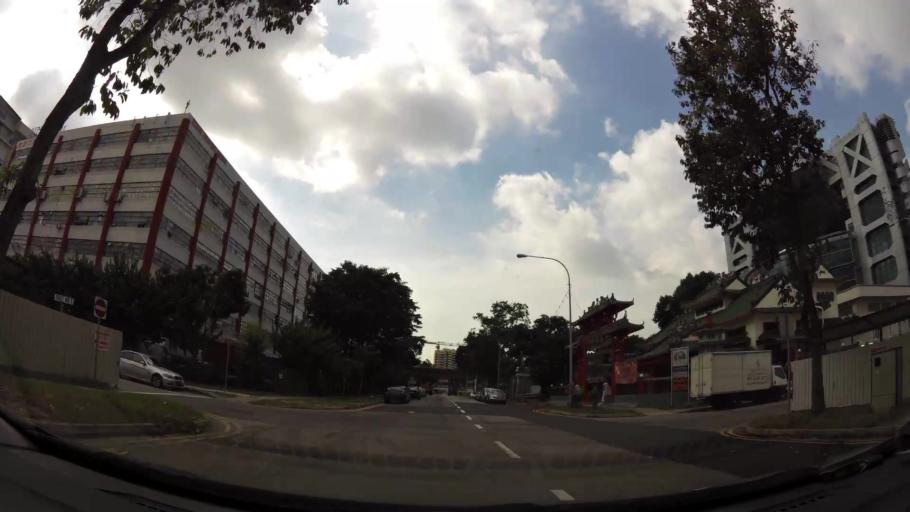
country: SG
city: Singapore
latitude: 1.3200
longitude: 103.8962
